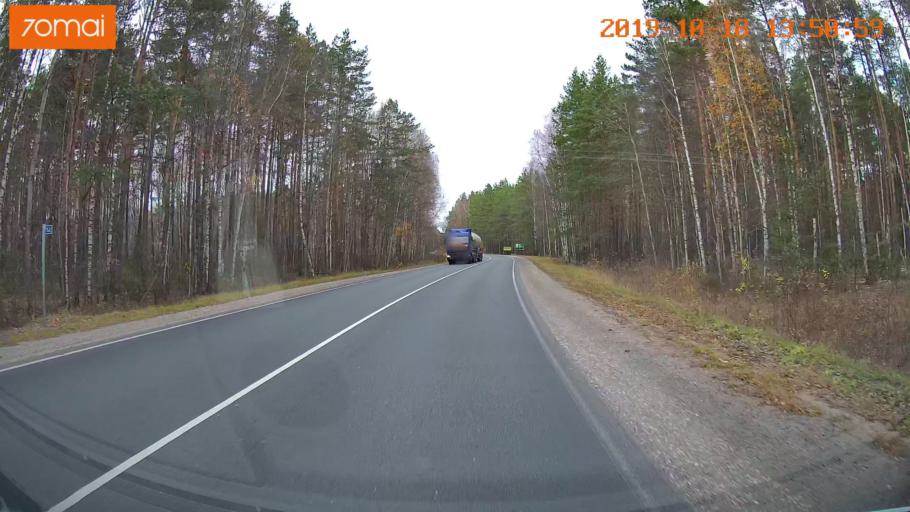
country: RU
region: Moskovskaya
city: Radovitskiy
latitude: 55.0124
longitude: 39.9645
